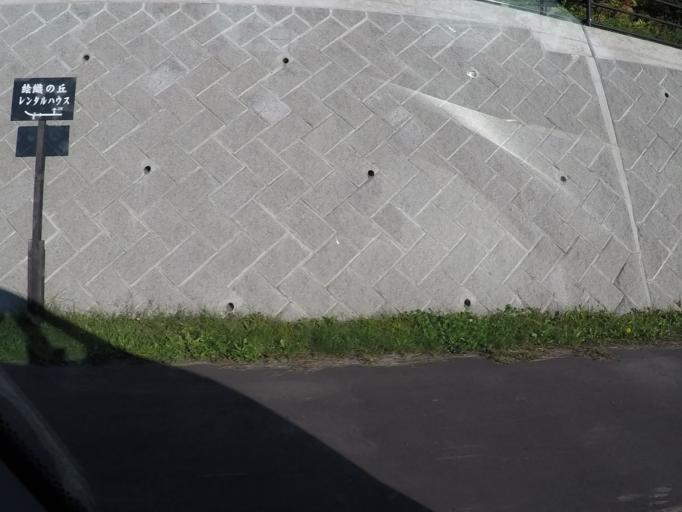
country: JP
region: Hokkaido
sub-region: Asahikawa-shi
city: Asahikawa
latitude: 43.6172
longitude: 142.4800
